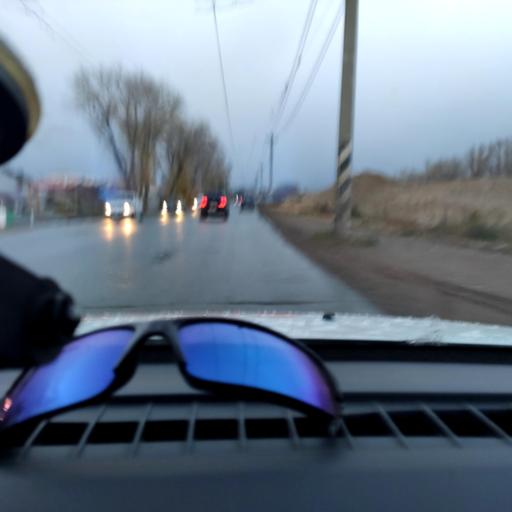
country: RU
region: Samara
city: Samara
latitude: 53.1431
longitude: 50.0980
